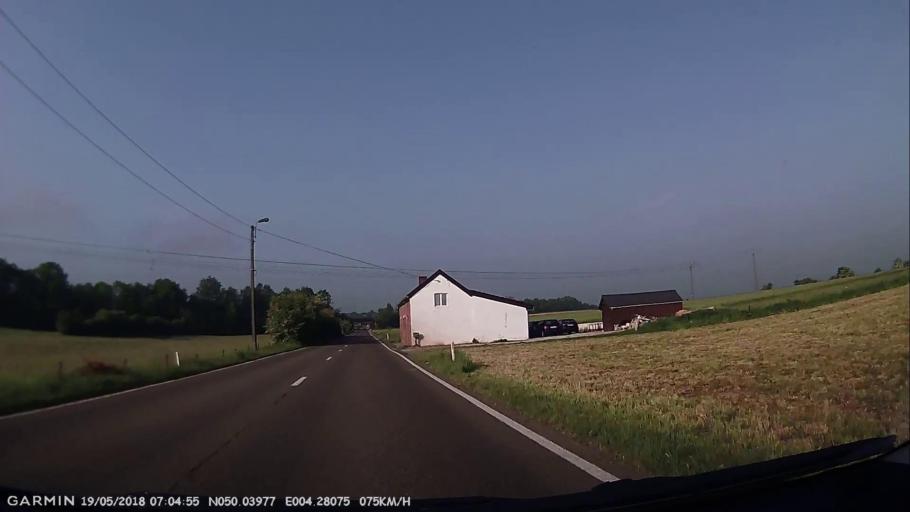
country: BE
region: Wallonia
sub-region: Province du Hainaut
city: Chimay
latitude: 50.0397
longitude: 4.2807
